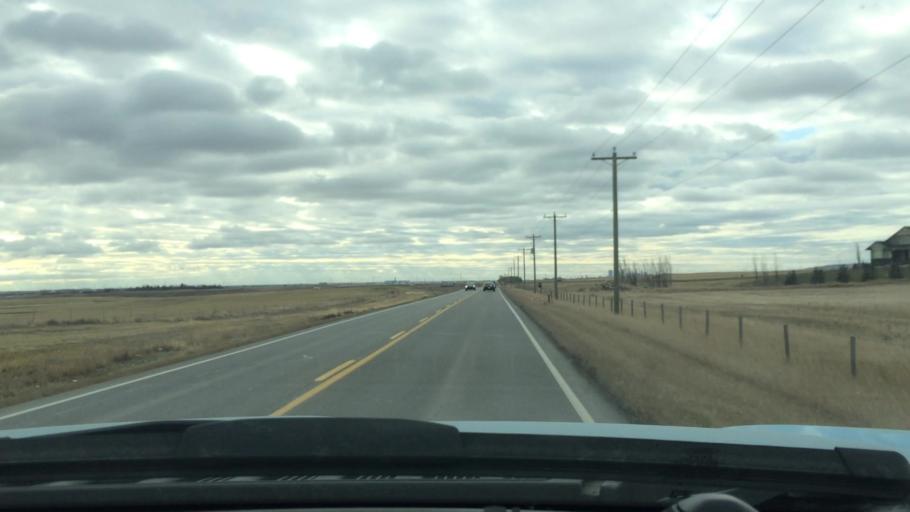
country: CA
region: Alberta
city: Airdrie
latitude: 51.2213
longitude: -114.0250
